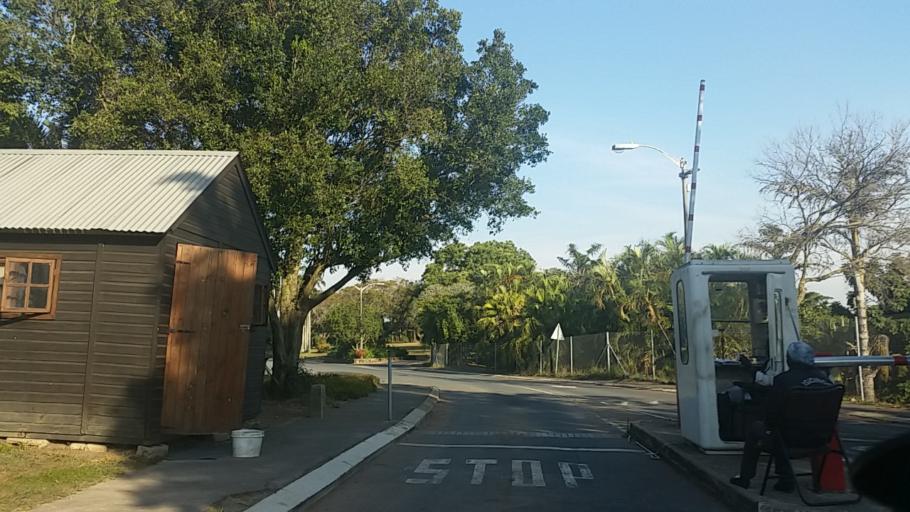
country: ZA
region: KwaZulu-Natal
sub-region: eThekwini Metropolitan Municipality
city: Berea
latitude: -29.8346
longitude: 30.9226
